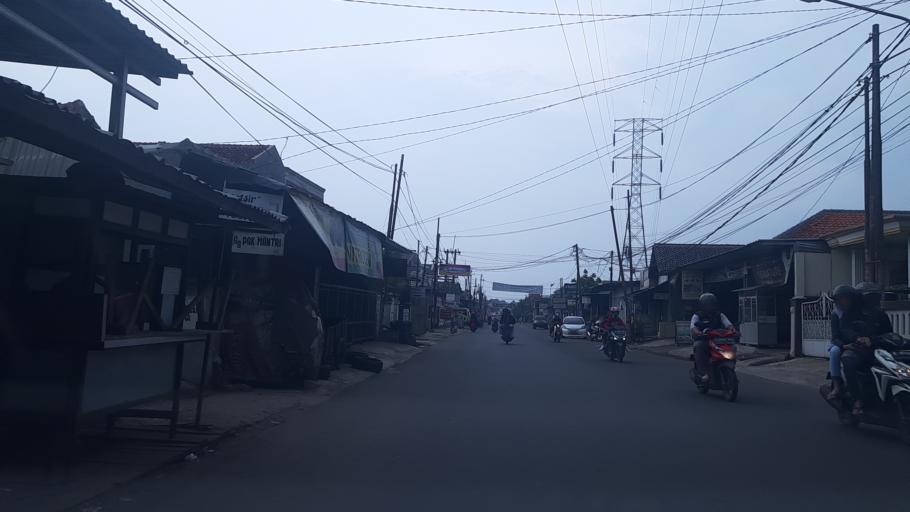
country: ID
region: West Java
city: Cibinong
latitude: -6.5236
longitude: 106.8584
